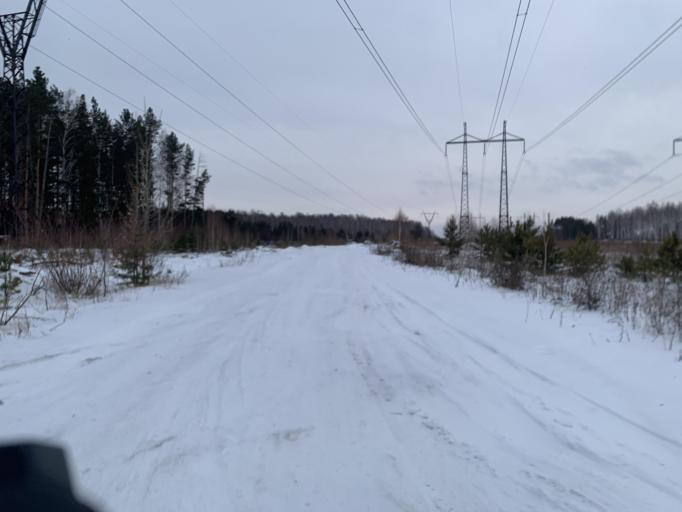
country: RU
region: Chelyabinsk
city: Roshchino
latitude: 55.1993
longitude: 61.2619
